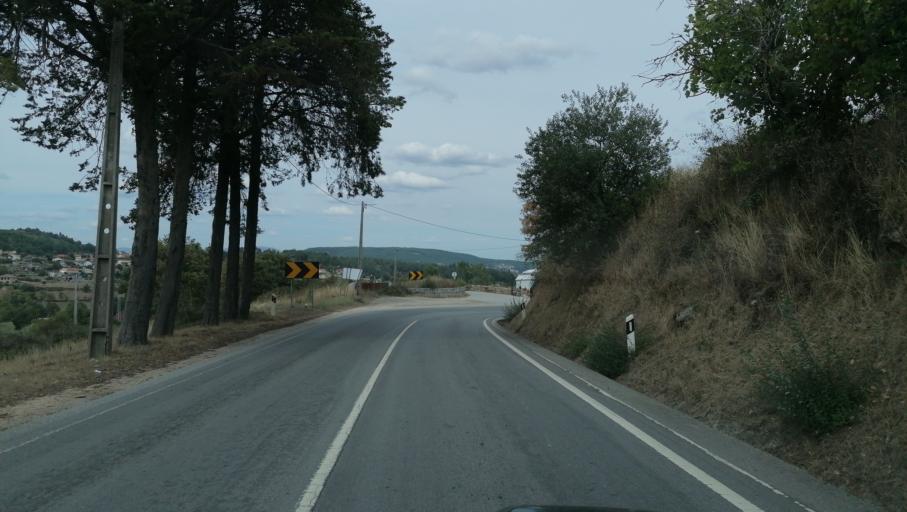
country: PT
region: Vila Real
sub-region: Vila Pouca de Aguiar
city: Vila Pouca de Aguiar
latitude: 41.5326
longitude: -7.6107
